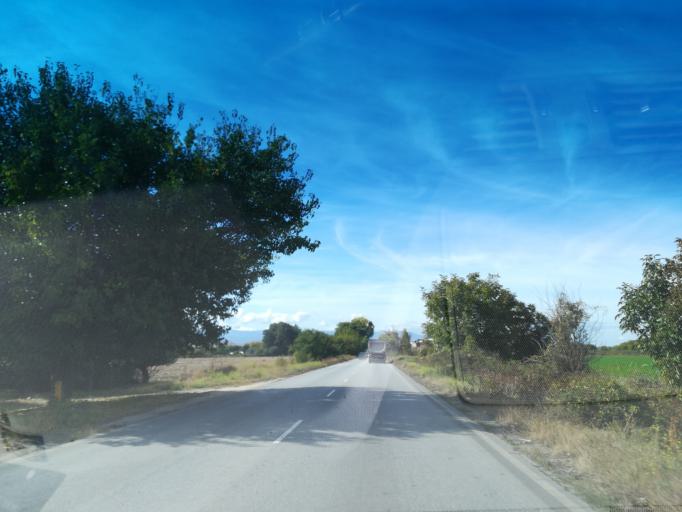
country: BG
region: Plovdiv
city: Stamboliyski
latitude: 42.1178
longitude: 24.5377
